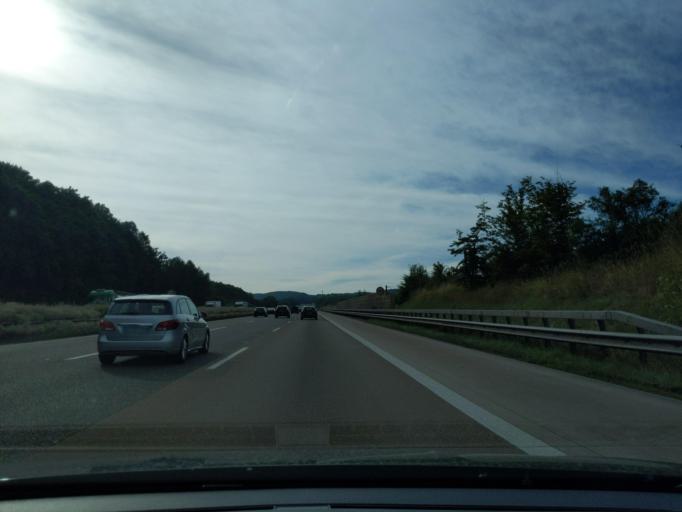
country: DE
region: Rheinland-Pfalz
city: Asbach
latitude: 50.6271
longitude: 7.4115
